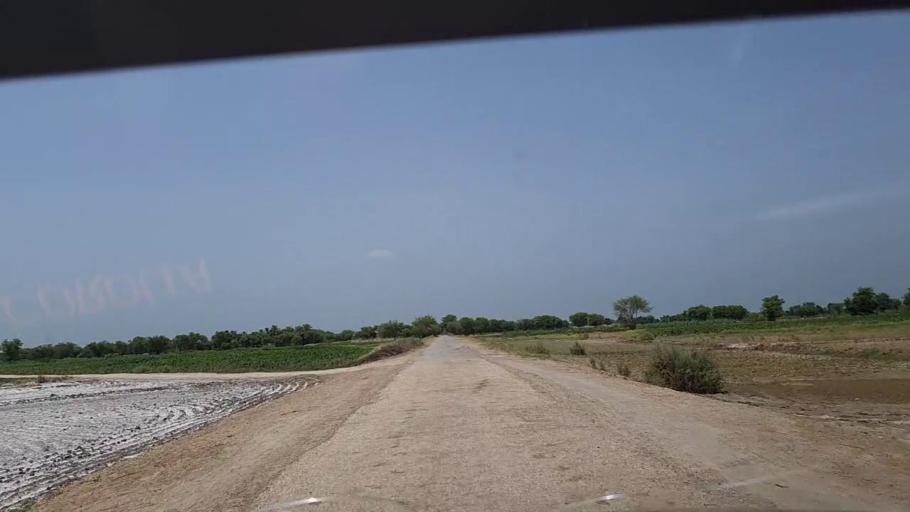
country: PK
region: Sindh
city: Khanpur
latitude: 27.7934
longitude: 69.4553
